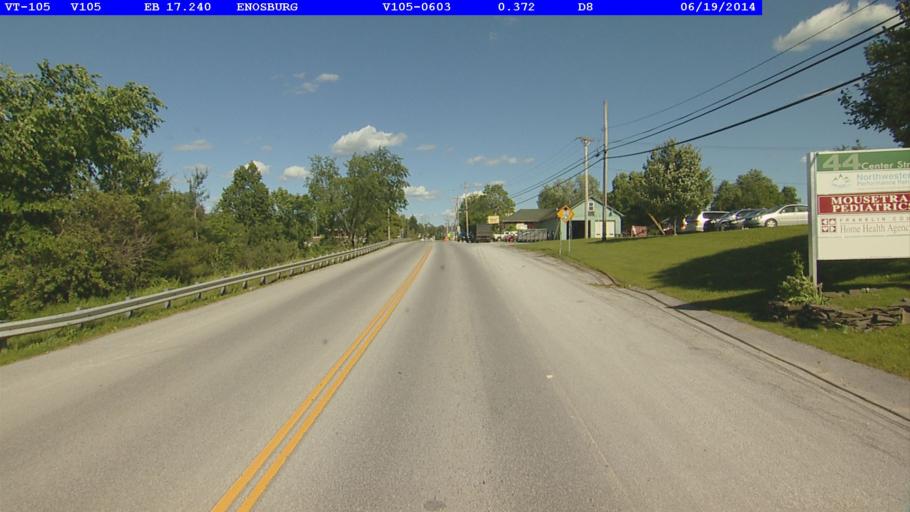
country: US
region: Vermont
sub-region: Franklin County
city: Enosburg Falls
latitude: 44.9057
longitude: -72.8128
